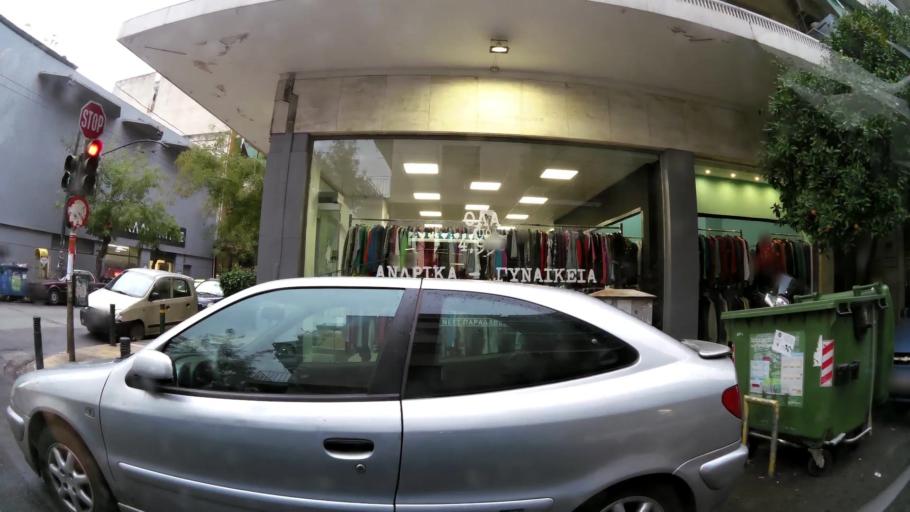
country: GR
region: Attica
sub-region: Nomarchia Athinas
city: Vyronas
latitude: 37.9639
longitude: 23.7475
